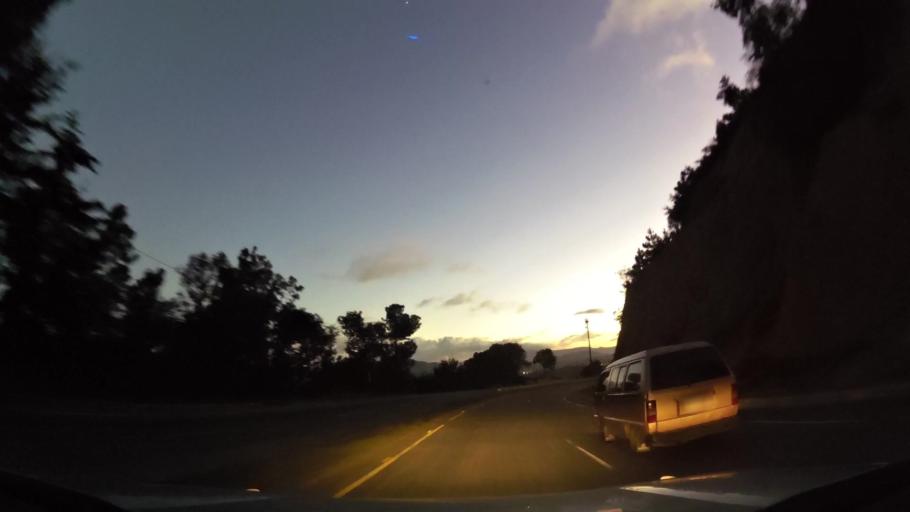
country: GT
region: Chimaltenango
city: Santa Apolonia
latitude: 14.7873
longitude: -90.9829
